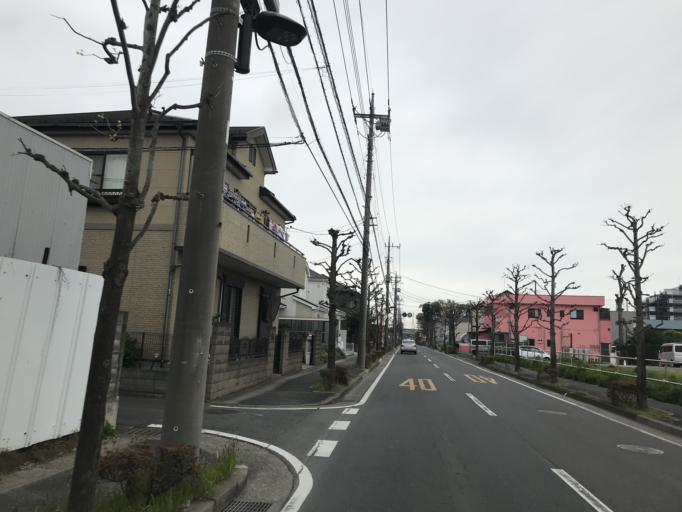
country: JP
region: Saitama
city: Yashio-shi
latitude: 35.8259
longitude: 139.8445
